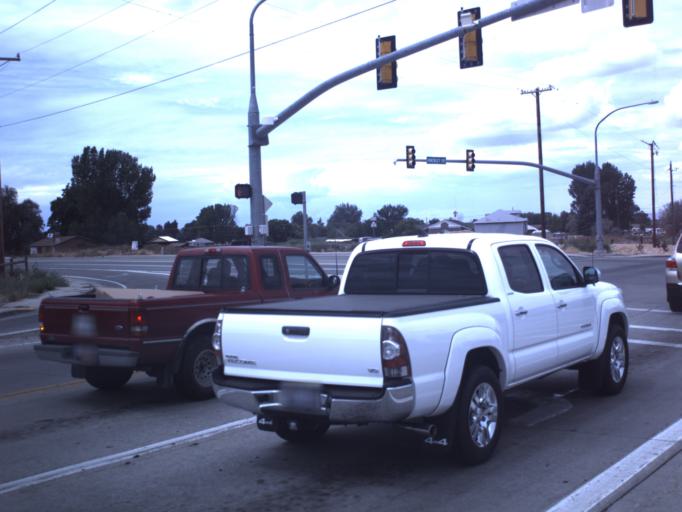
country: US
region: Utah
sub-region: Weber County
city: West Haven
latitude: 41.1976
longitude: -112.0397
